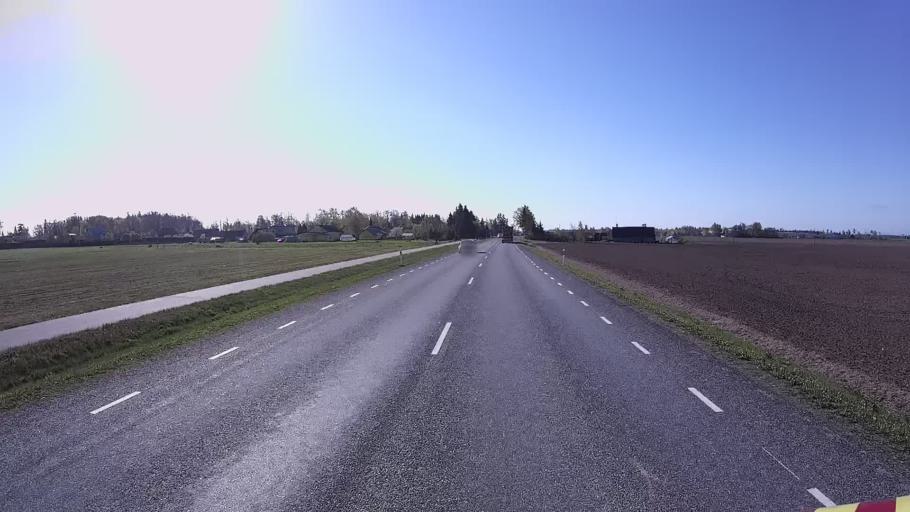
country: EE
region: Jaervamaa
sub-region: Paide linn
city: Paide
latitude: 58.7592
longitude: 25.5548
